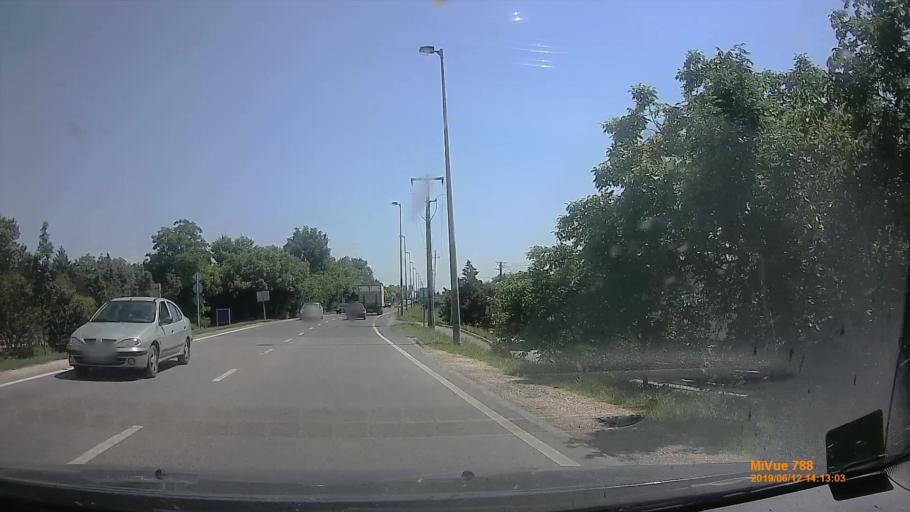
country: HU
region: Csongrad
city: Szeged
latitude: 46.2353
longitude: 20.1720
